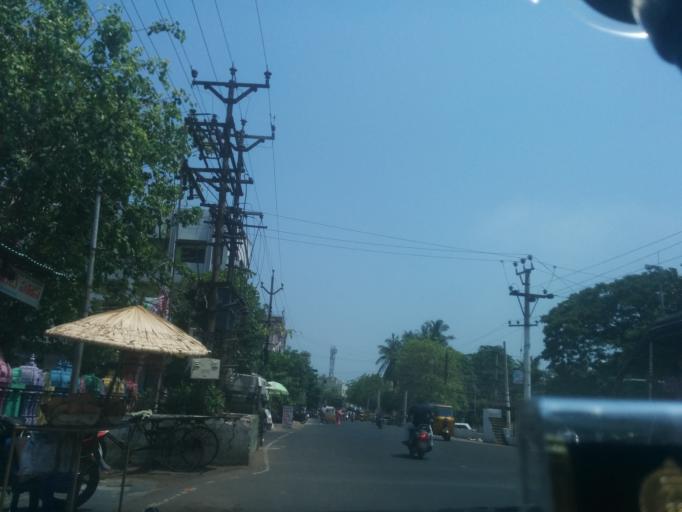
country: IN
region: Andhra Pradesh
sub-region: East Godavari
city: Rajahmundry
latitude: 17.0146
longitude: 81.7721
